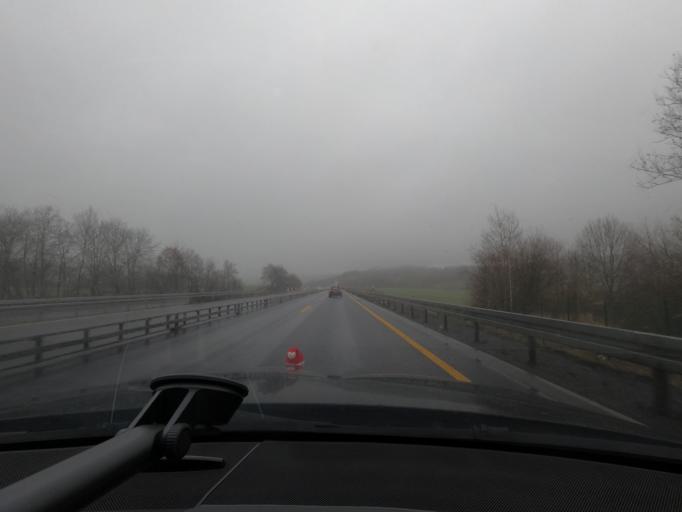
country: DE
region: Lower Saxony
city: Hillerse
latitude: 51.6762
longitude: 9.9248
